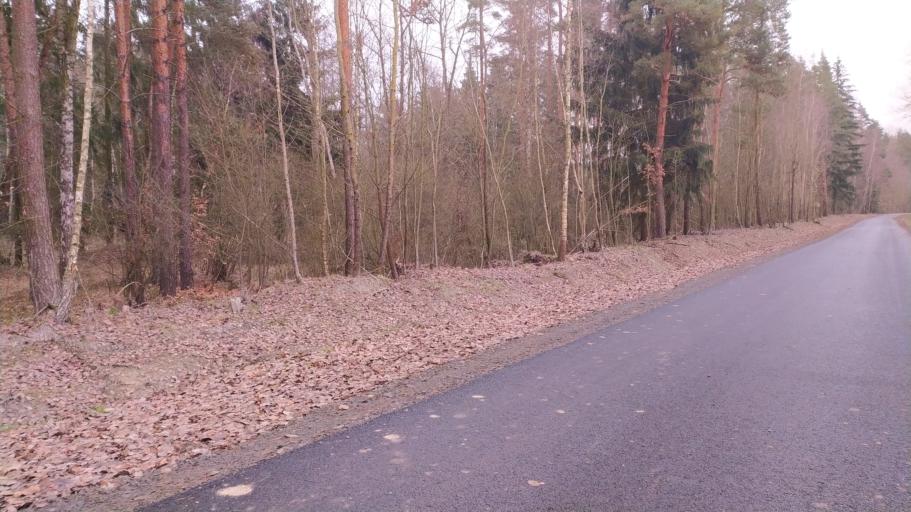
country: DE
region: Bavaria
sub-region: Upper Franconia
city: Schirnding
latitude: 50.1005
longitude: 12.2726
